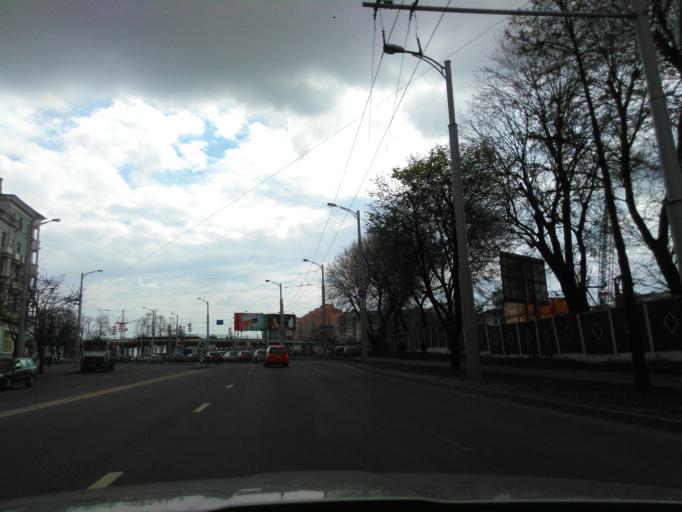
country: BY
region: Minsk
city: Minsk
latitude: 53.8942
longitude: 27.5399
